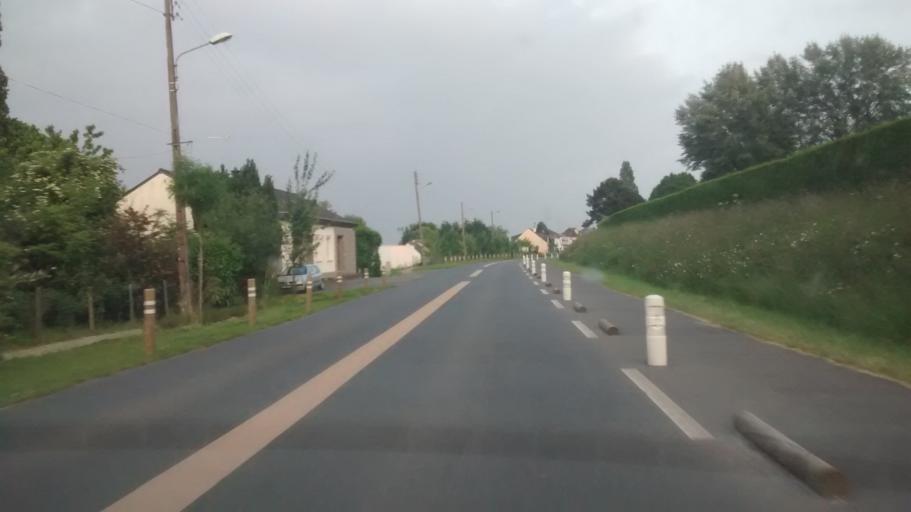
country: FR
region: Brittany
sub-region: Departement du Morbihan
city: Guer
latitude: 47.9472
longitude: -2.1337
